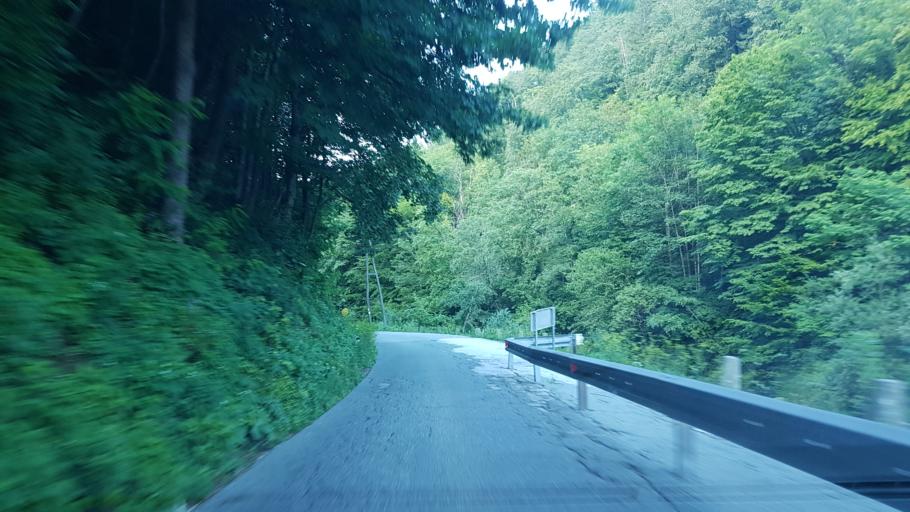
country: SI
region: Ziri
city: Ziri
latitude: 46.0883
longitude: 14.0955
